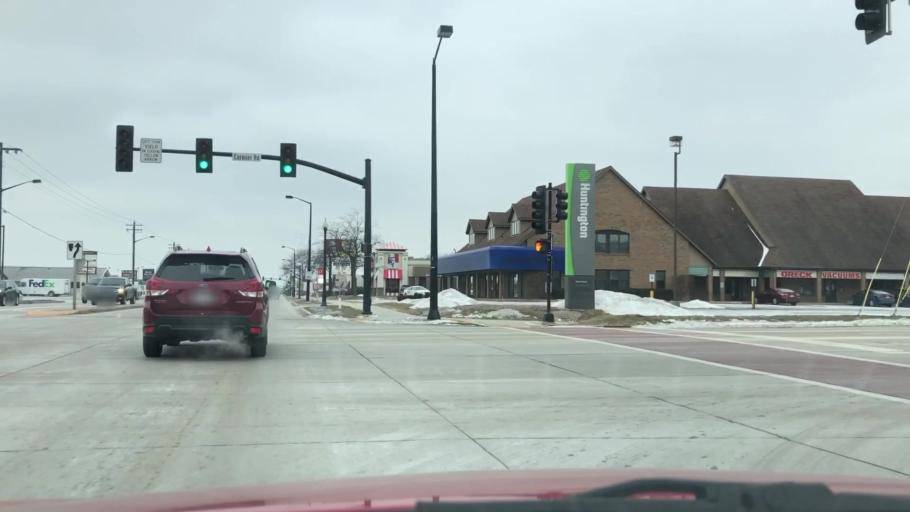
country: US
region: Wisconsin
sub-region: Brown County
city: Ashwaubenon
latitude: 44.4897
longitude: -88.0652
